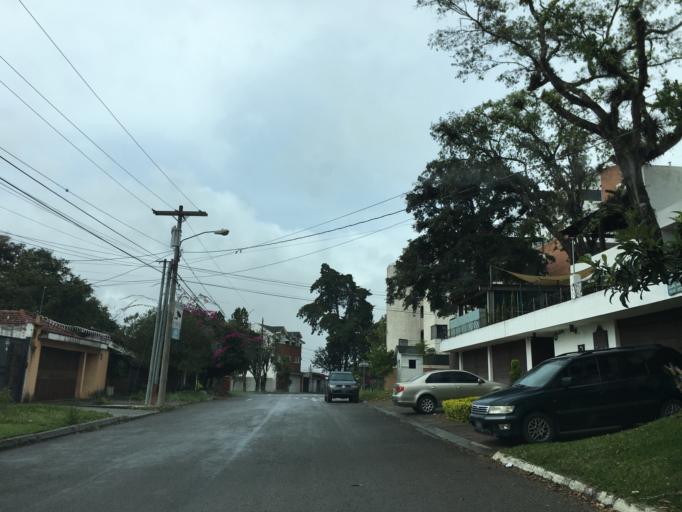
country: GT
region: Guatemala
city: Santa Catarina Pinula
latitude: 14.5901
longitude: -90.4961
